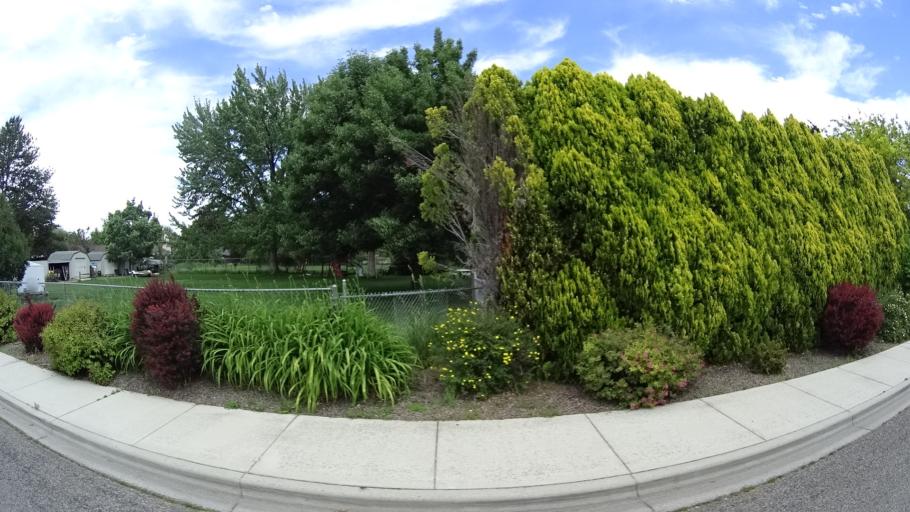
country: US
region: Idaho
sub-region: Ada County
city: Eagle
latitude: 43.6412
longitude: -116.3286
